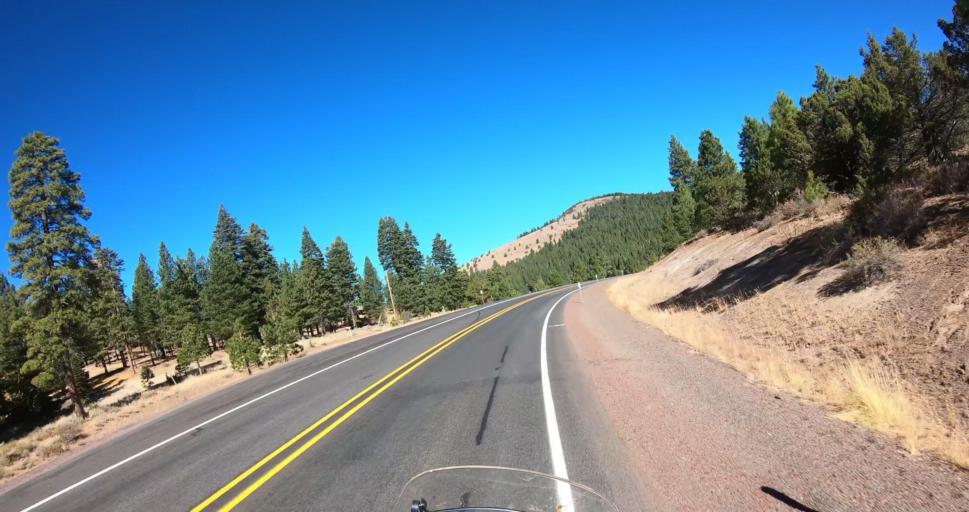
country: US
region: Oregon
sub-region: Lake County
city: Lakeview
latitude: 42.2333
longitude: -120.2919
